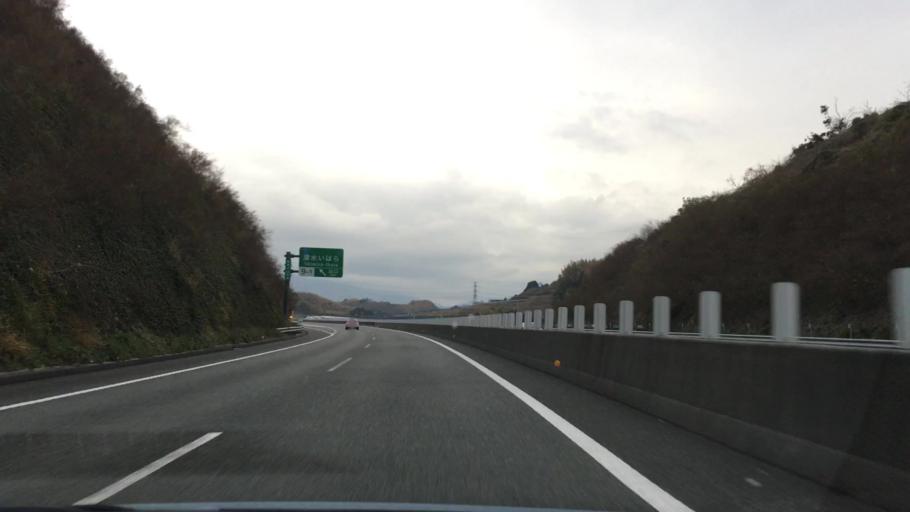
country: JP
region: Shizuoka
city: Shizuoka-shi
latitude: 35.0660
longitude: 138.4802
